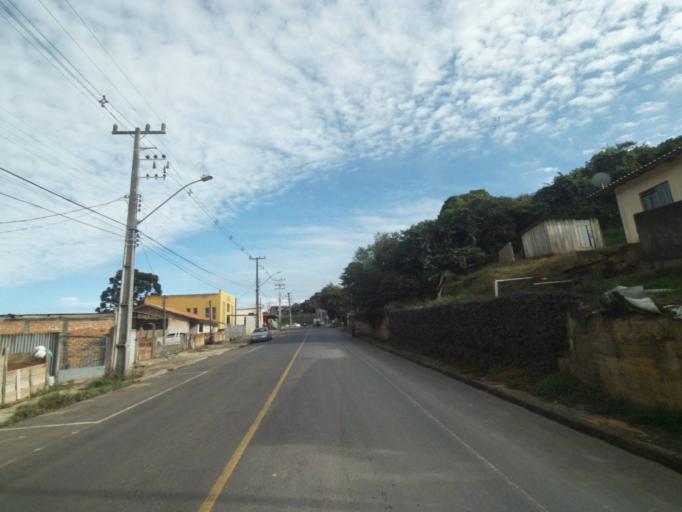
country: BR
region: Parana
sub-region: Telemaco Borba
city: Telemaco Borba
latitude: -24.3404
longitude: -50.6145
